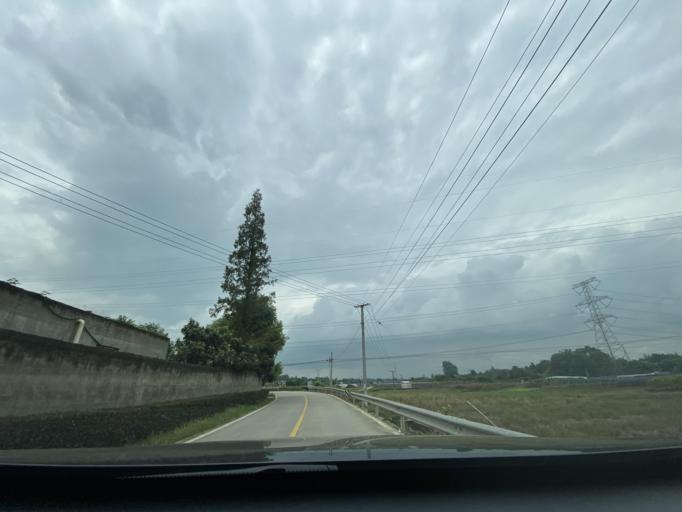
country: CN
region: Sichuan
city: Wujin
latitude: 30.3734
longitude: 103.9701
